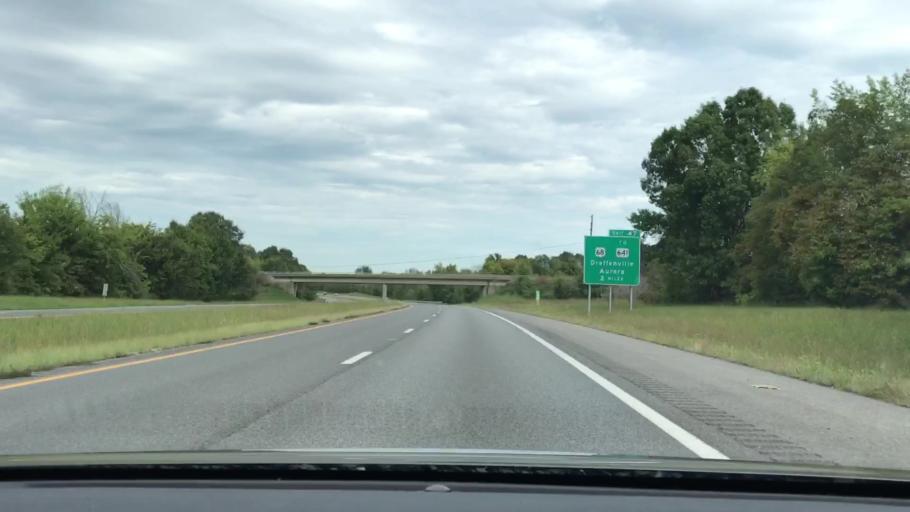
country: US
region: Kentucky
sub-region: Marshall County
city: Benton
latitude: 36.8996
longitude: -88.3474
